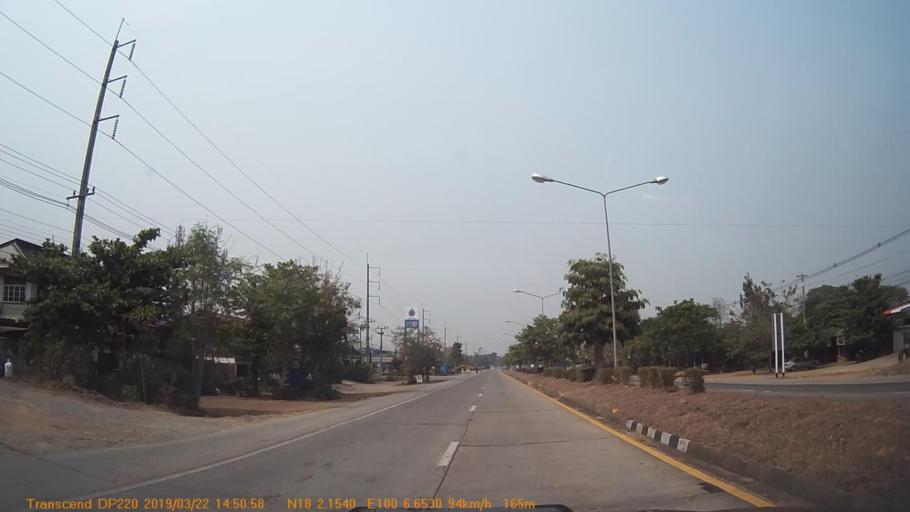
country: TH
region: Phrae
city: Sung Men
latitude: 18.0361
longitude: 100.1109
